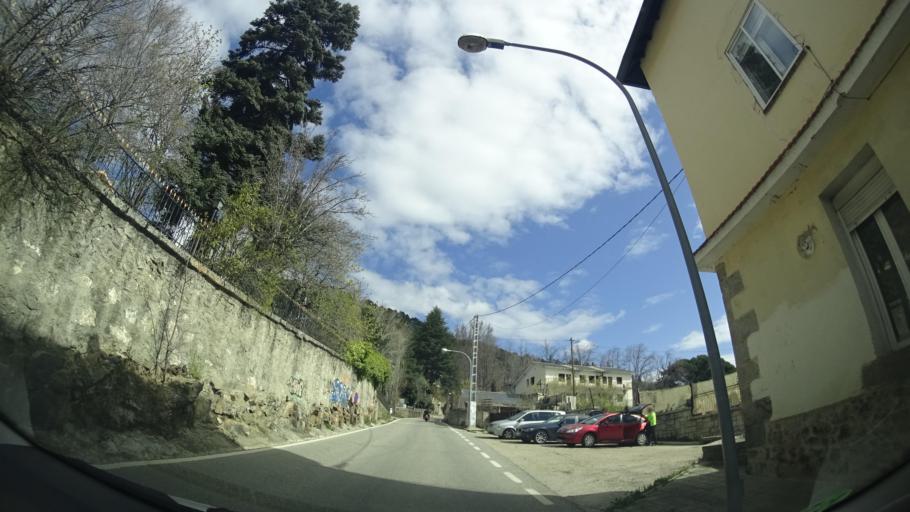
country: ES
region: Madrid
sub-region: Provincia de Madrid
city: Miraflores de la Sierra
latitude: 40.8139
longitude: -3.7699
